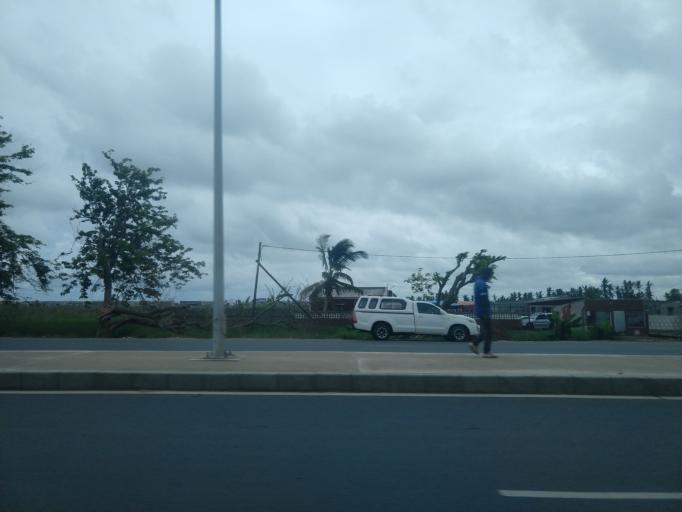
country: MZ
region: Sofala
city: Beira
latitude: -19.7867
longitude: 34.8756
